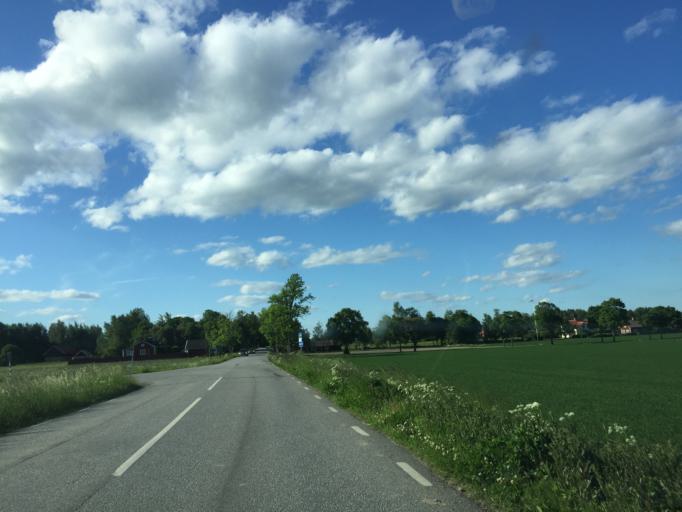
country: SE
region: OErebro
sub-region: Orebro Kommun
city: Orebro
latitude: 59.1976
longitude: 15.2468
